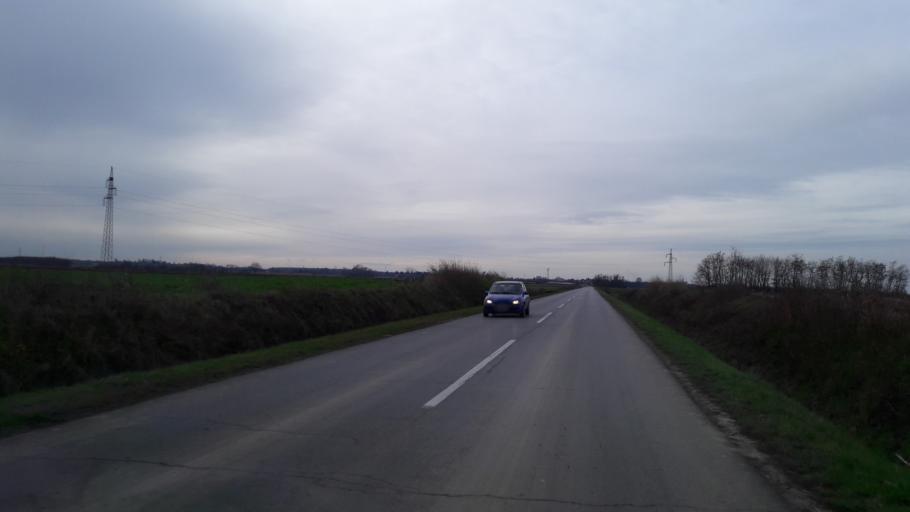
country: HR
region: Osjecko-Baranjska
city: Semeljci
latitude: 45.3771
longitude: 18.5570
